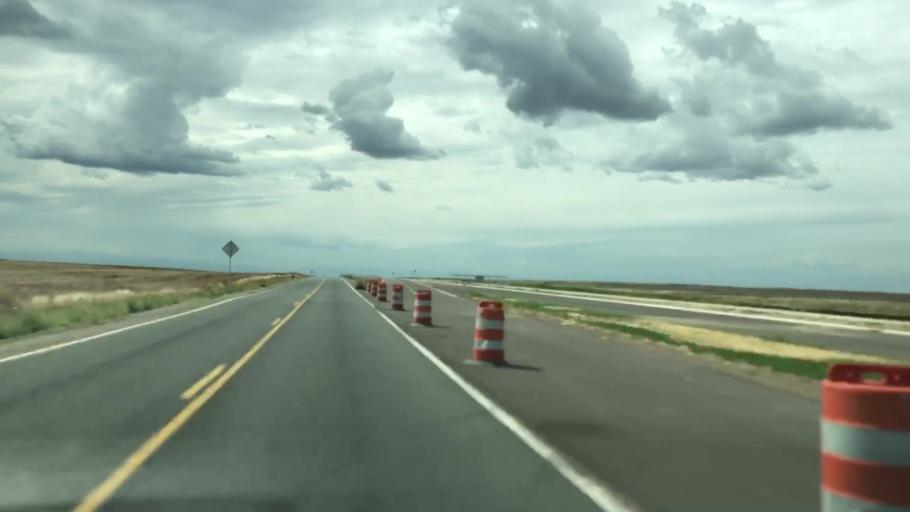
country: US
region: Colorado
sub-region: Adams County
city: Aurora
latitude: 39.7981
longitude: -104.6694
